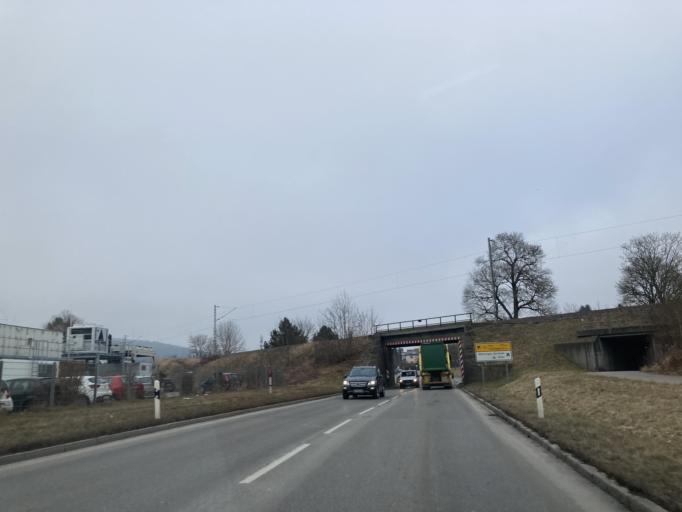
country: DE
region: Baden-Wuerttemberg
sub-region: Freiburg Region
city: Wurmlingen
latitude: 47.9636
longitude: 8.7839
